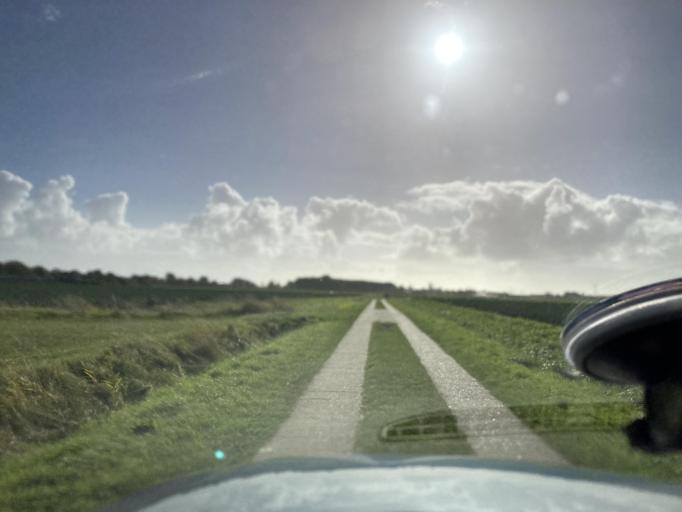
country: DE
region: Schleswig-Holstein
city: Oesterdeichstrich
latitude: 54.1432
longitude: 8.8908
